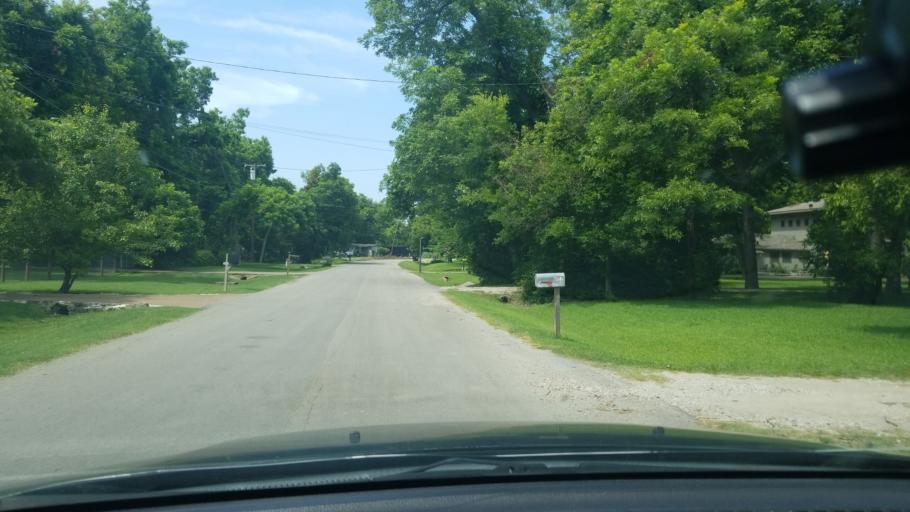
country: US
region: Texas
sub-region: Dallas County
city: Highland Park
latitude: 32.8082
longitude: -96.7134
